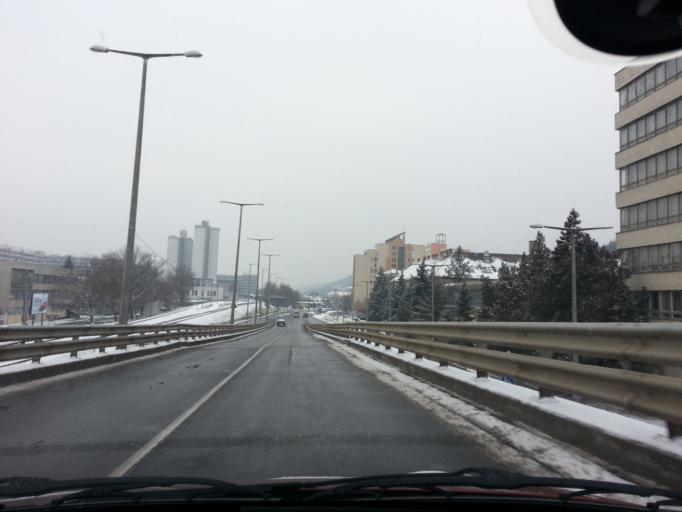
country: HU
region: Nograd
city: Salgotarjan
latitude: 48.1076
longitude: 19.8088
